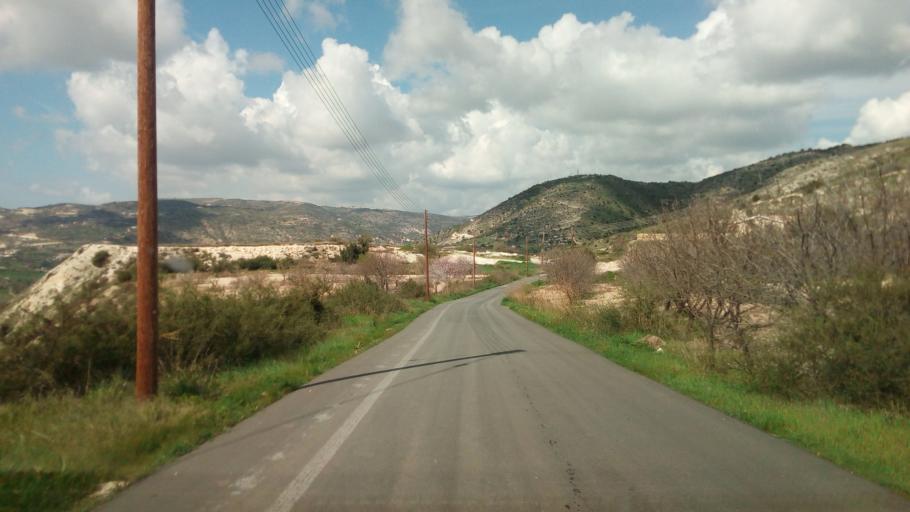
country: CY
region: Pafos
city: Mesogi
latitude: 34.7848
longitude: 32.5465
